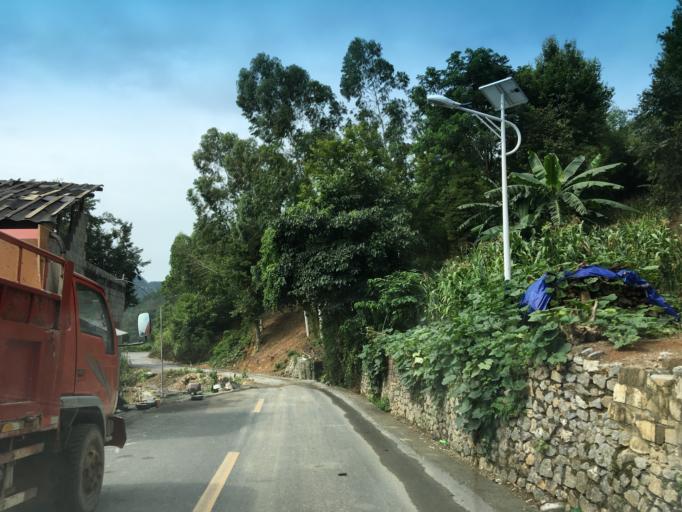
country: CN
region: Guangxi Zhuangzu Zizhiqu
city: Xinzhou
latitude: 24.8214
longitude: 105.6436
